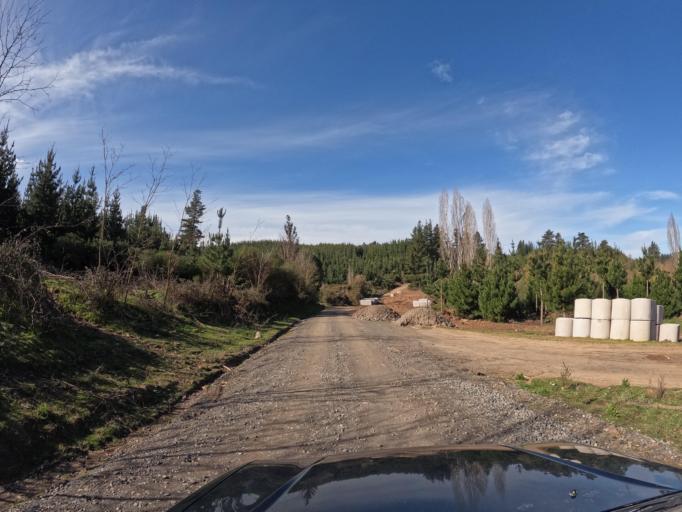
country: CL
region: Biobio
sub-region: Provincia de Biobio
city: La Laja
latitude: -37.0882
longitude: -72.7763
